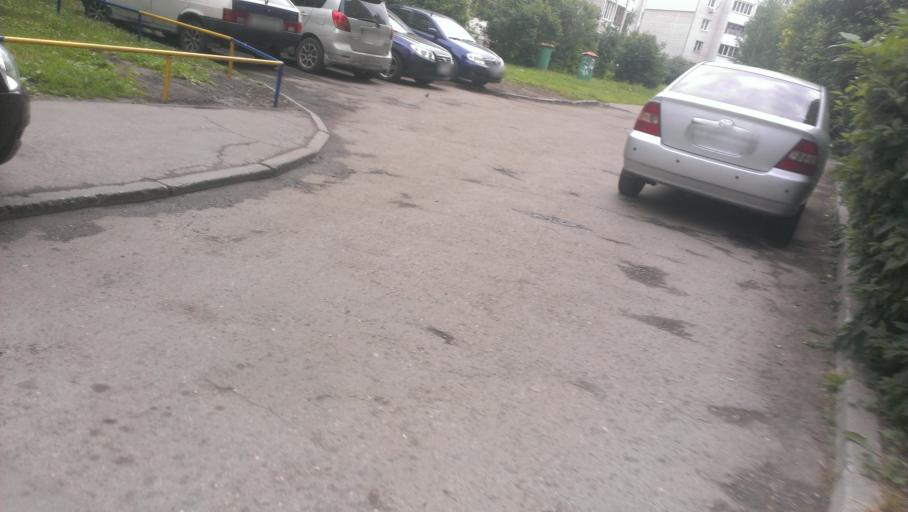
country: RU
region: Altai Krai
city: Novosilikatnyy
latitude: 53.3343
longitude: 83.6745
